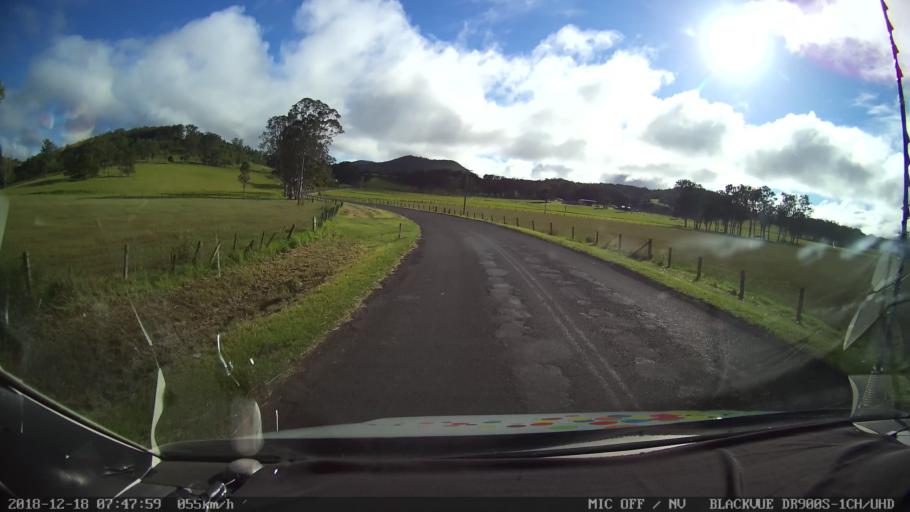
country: AU
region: New South Wales
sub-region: Kyogle
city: Kyogle
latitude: -28.4616
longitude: 152.5620
